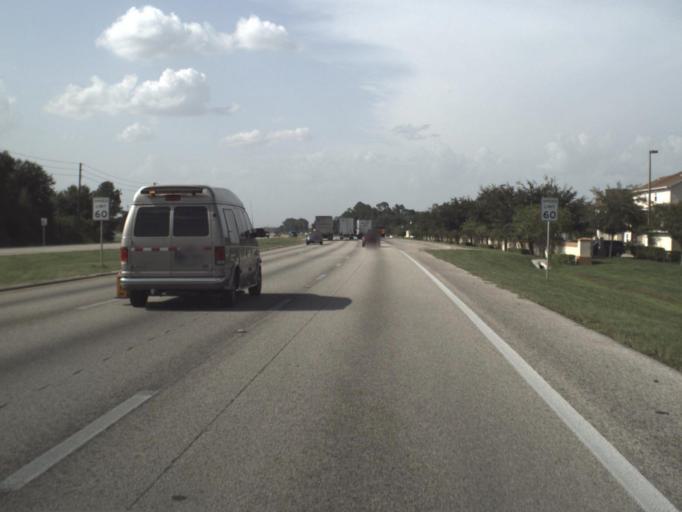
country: US
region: Florida
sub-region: Polk County
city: Lake Wales
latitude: 27.9301
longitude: -81.6079
